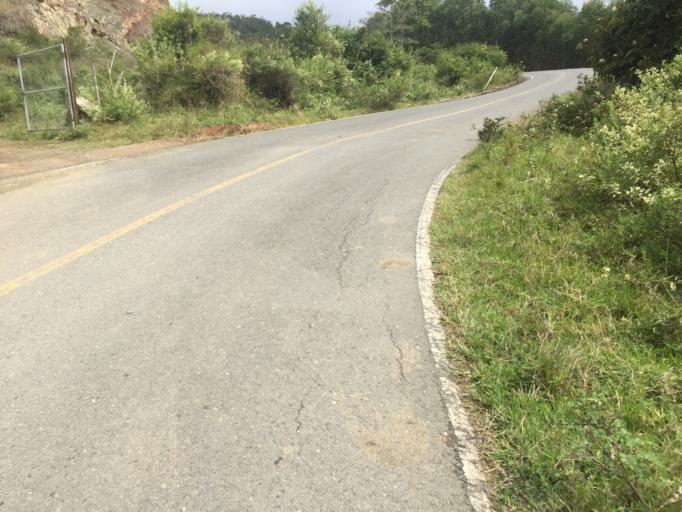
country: CO
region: Valle del Cauca
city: Dagua
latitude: 3.7018
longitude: -76.5877
